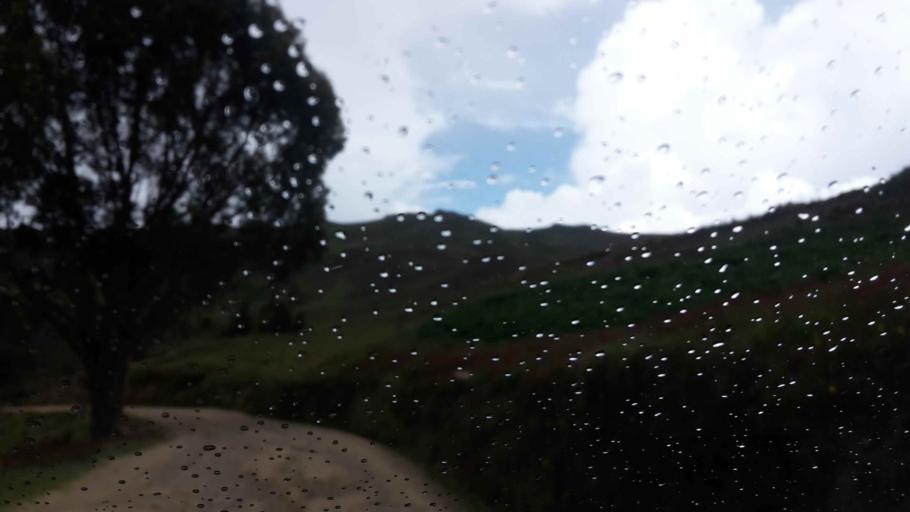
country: BO
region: Cochabamba
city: Cochabamba
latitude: -17.1368
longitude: -66.1063
